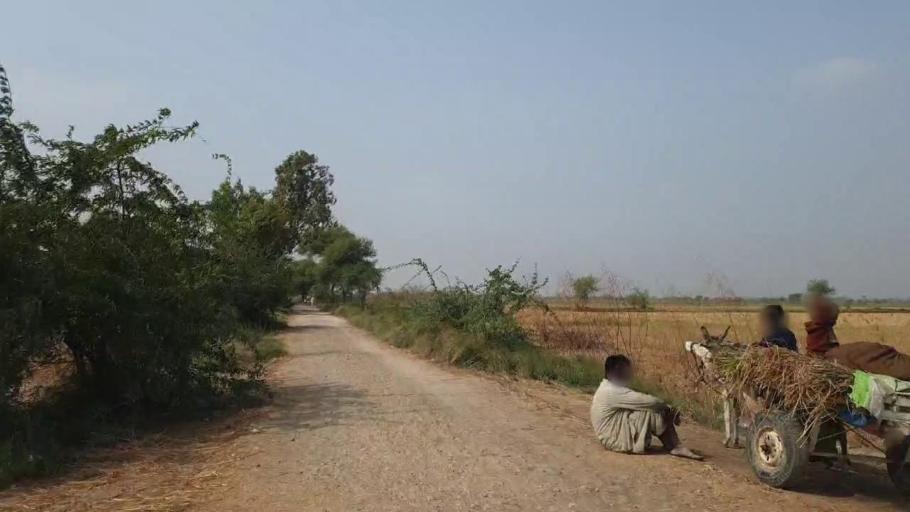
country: PK
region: Sindh
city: Kario
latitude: 24.7602
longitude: 68.5368
